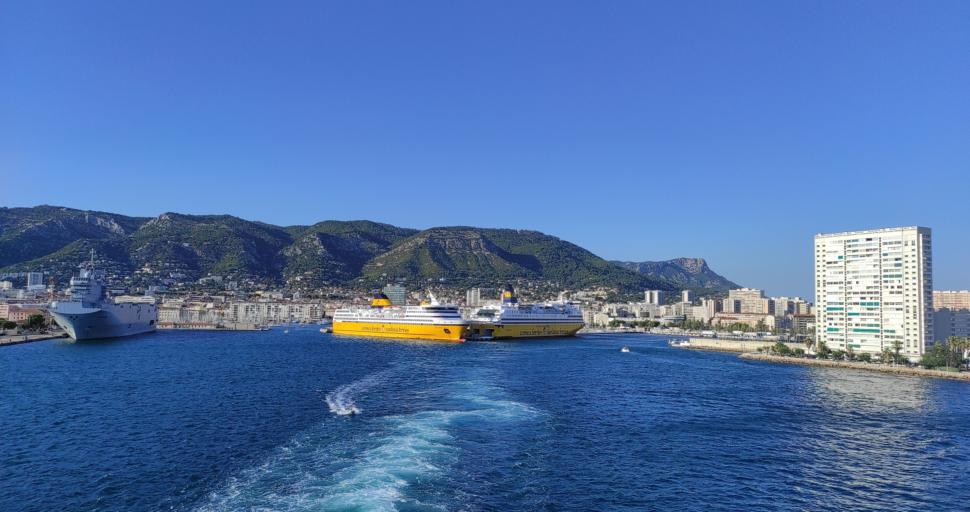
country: FR
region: Provence-Alpes-Cote d'Azur
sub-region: Departement du Var
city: Toulon
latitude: 43.1118
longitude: 5.9266
